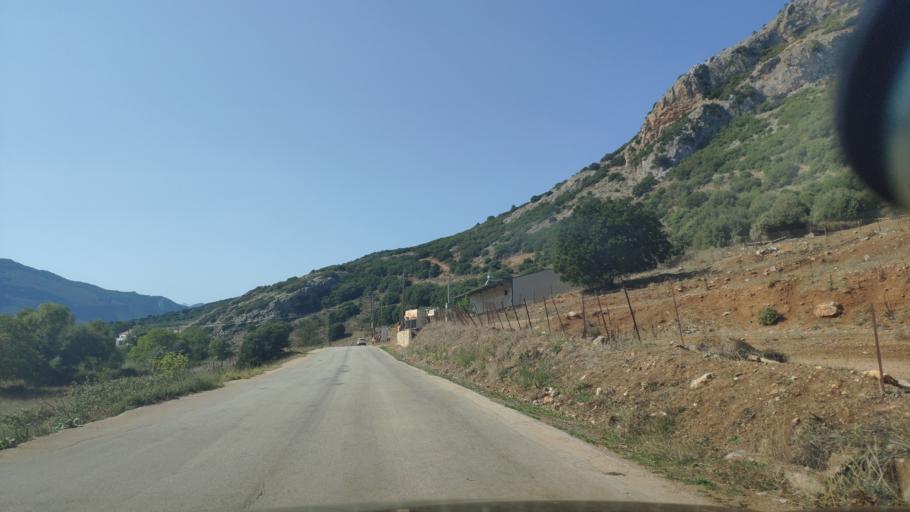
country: GR
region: Peloponnese
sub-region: Nomos Korinthias
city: Nemea
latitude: 37.9008
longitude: 22.5200
